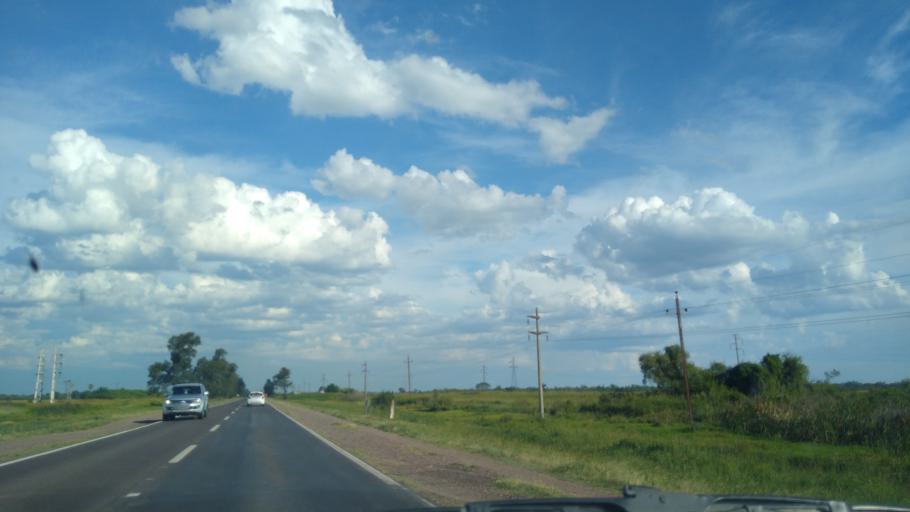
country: AR
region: Chaco
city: Presidencia Roque Saenz Pena
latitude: -26.8180
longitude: -60.4028
